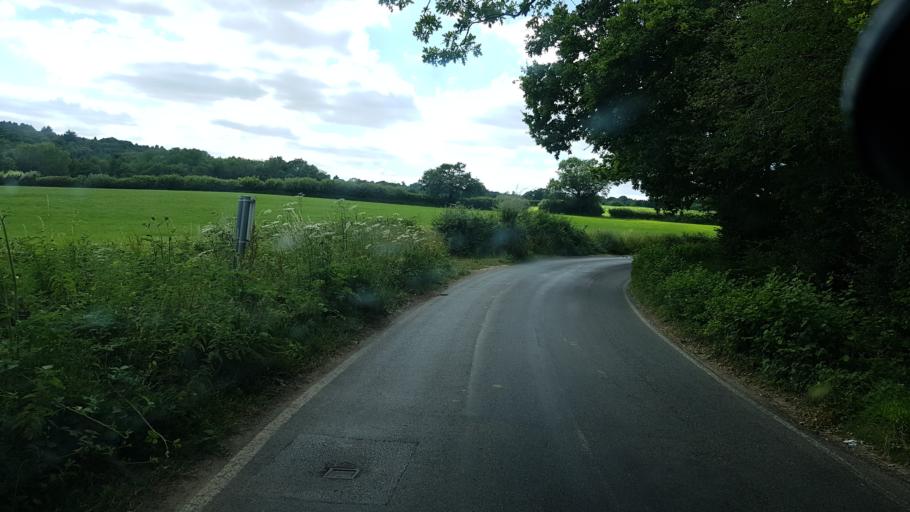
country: GB
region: England
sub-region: West Sussex
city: Maidenbower
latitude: 51.0630
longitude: -0.1421
